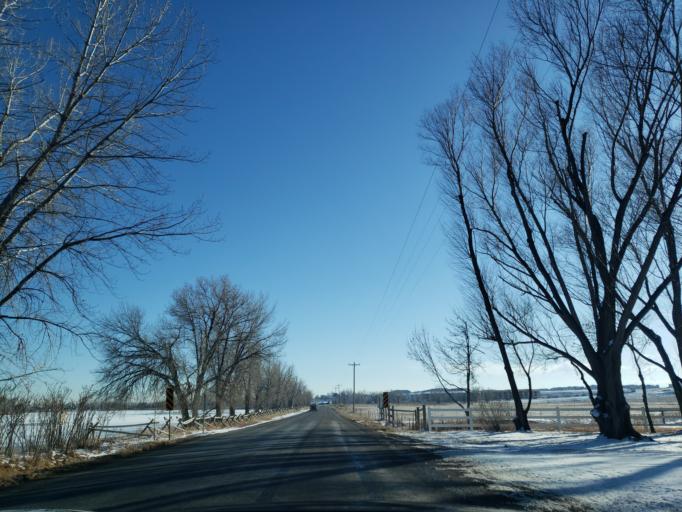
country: US
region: Colorado
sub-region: Larimer County
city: Fort Collins
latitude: 40.5287
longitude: -105.0013
